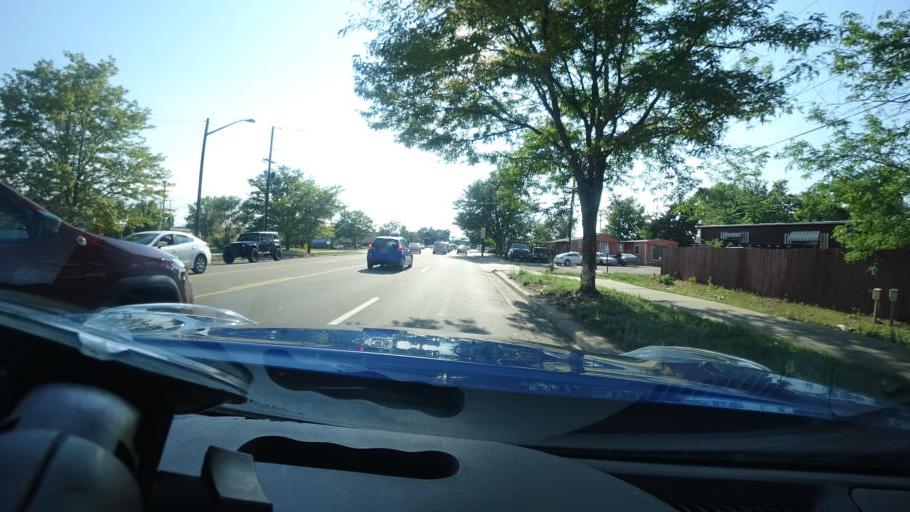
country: US
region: Colorado
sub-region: Arapahoe County
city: Sheridan
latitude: 39.6787
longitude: -105.0222
